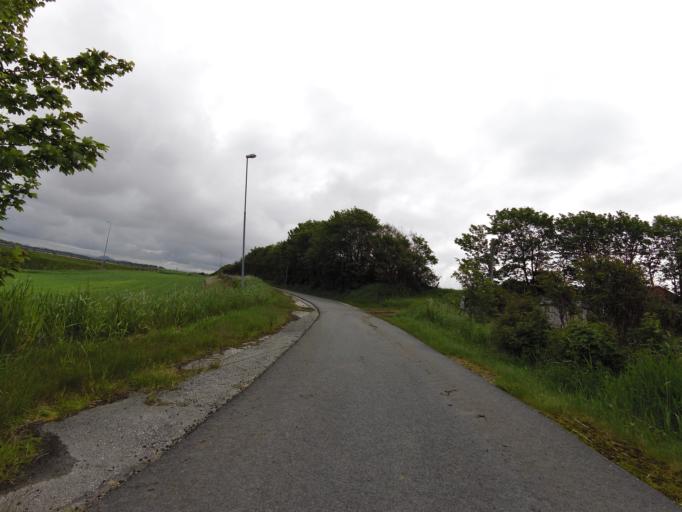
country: NO
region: Rogaland
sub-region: Klepp
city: Kleppe
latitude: 58.8202
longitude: 5.5876
